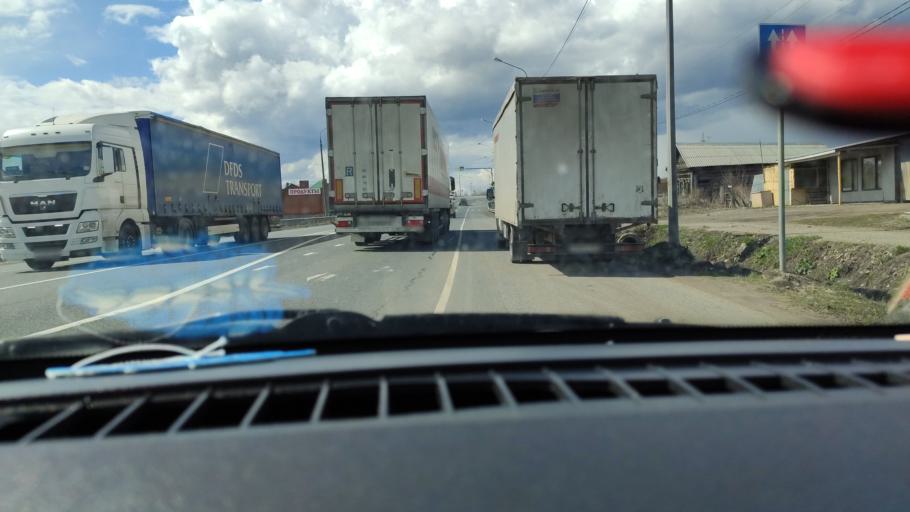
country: RU
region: Samara
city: Mezhdurechensk
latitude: 53.2490
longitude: 49.1657
